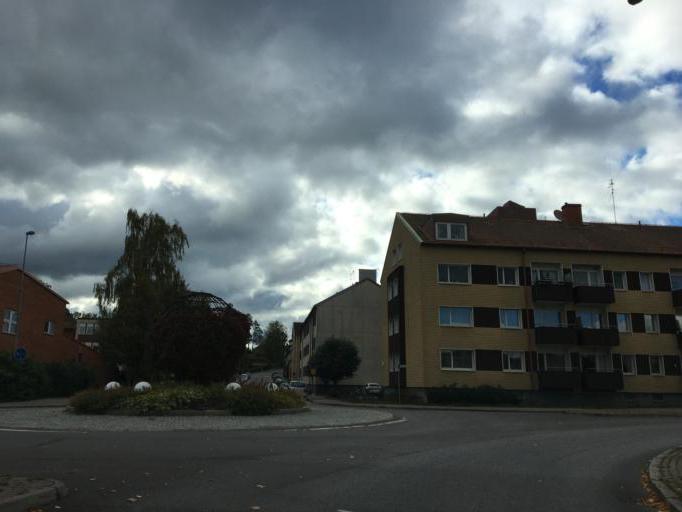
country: SE
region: Soedermanland
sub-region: Katrineholms Kommun
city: Katrineholm
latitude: 58.9939
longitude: 16.2013
